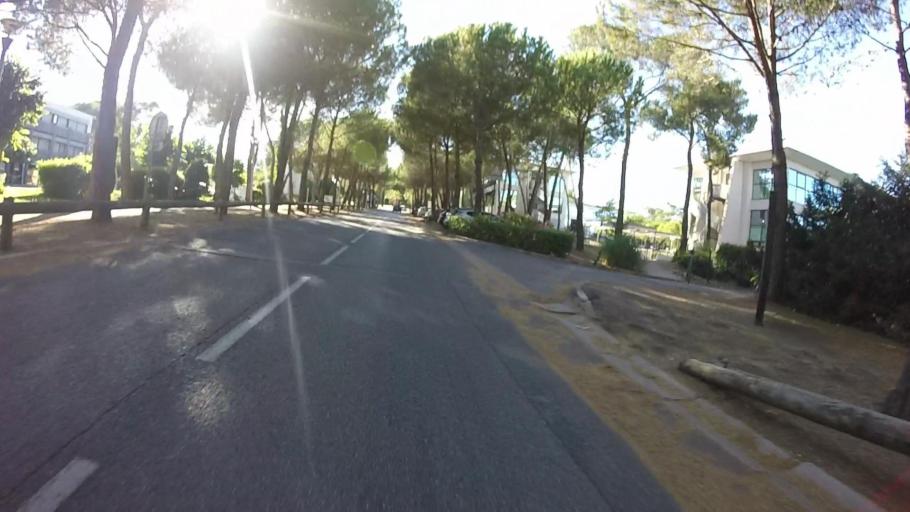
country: FR
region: Provence-Alpes-Cote d'Azur
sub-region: Departement des Alpes-Maritimes
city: Mougins
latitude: 43.6105
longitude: 7.0145
